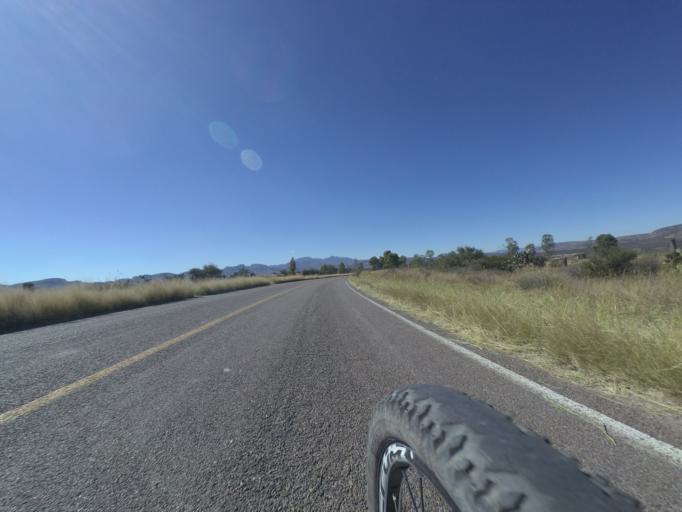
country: MX
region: Aguascalientes
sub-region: Aguascalientes
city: Los Canos
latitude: 21.8654
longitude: -102.5023
